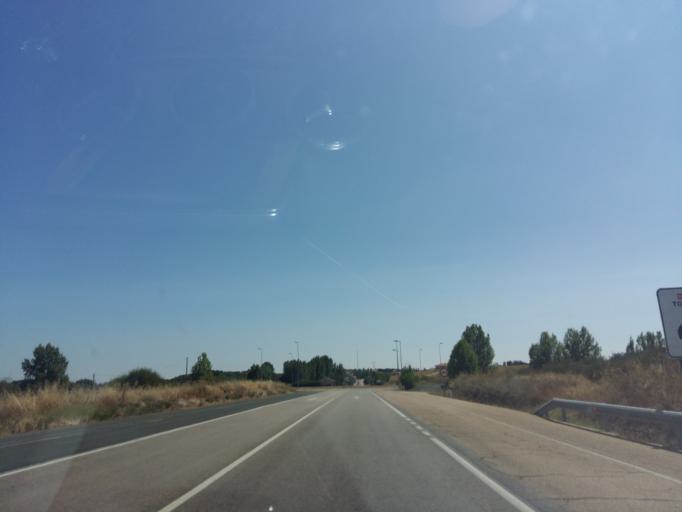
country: ES
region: Castille and Leon
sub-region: Provincia de Leon
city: San Justo de la Vega
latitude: 42.4367
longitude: -6.0337
